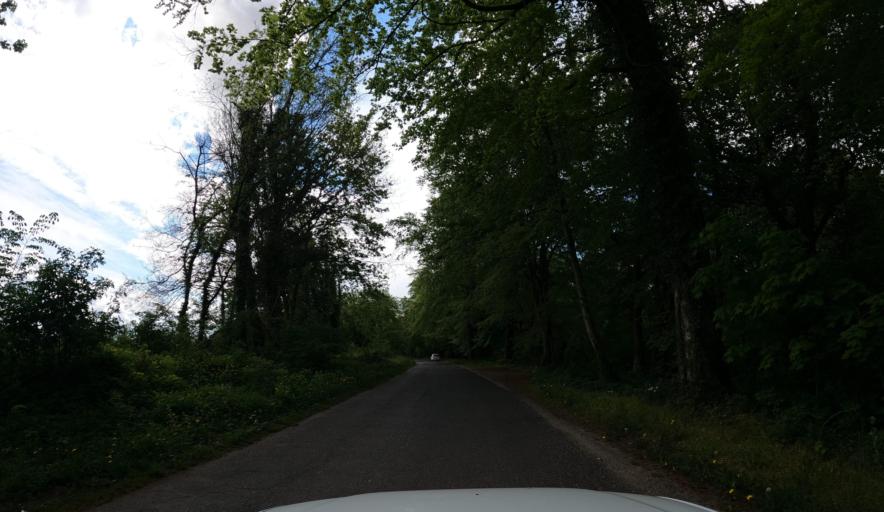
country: PL
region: West Pomeranian Voivodeship
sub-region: Powiat kamienski
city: Wolin
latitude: 53.8522
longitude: 14.6310
